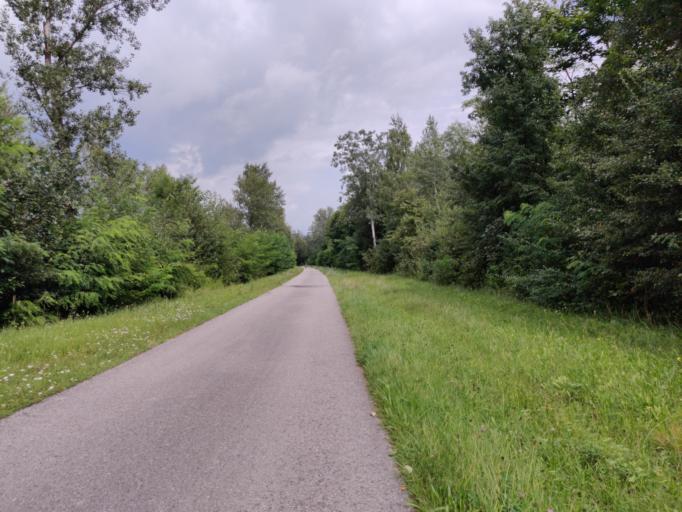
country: AT
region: Lower Austria
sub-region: Politischer Bezirk Melk
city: Melk
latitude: 48.2241
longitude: 15.3132
